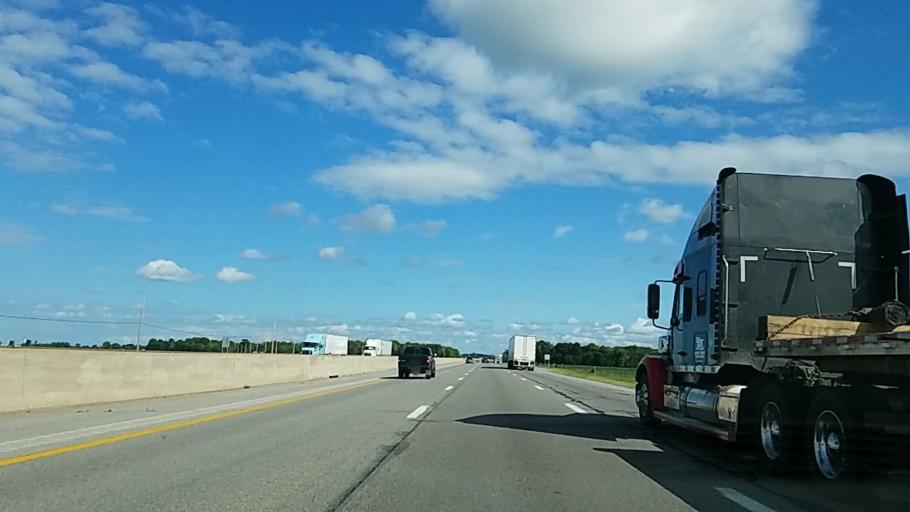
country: US
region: Ohio
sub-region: Sandusky County
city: Stony Prairie
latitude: 41.4297
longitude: -83.2011
